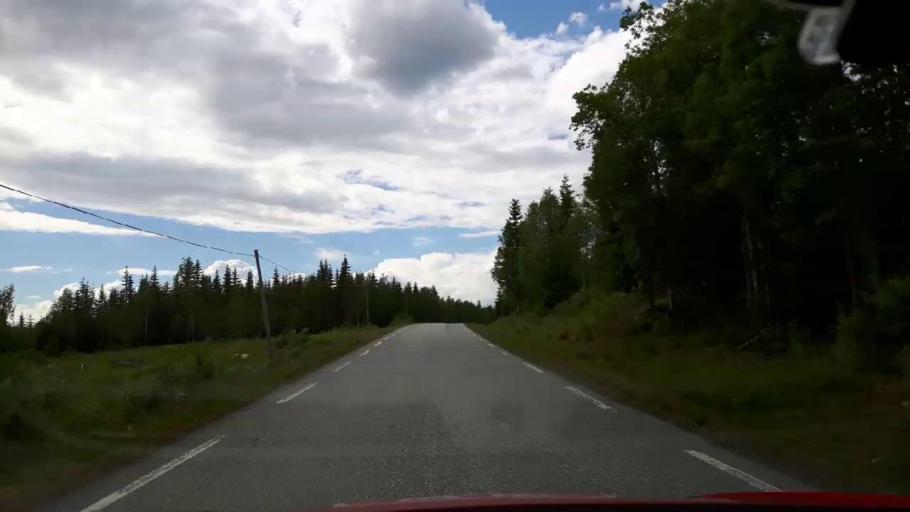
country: NO
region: Nord-Trondelag
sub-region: Lierne
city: Sandvika
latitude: 64.1177
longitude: 13.9521
